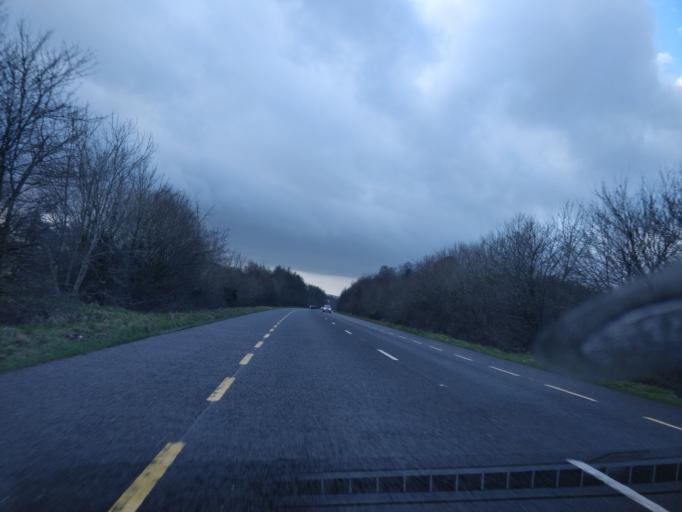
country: IE
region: Connaught
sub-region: Maigh Eo
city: Swinford
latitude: 53.9312
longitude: -8.9486
